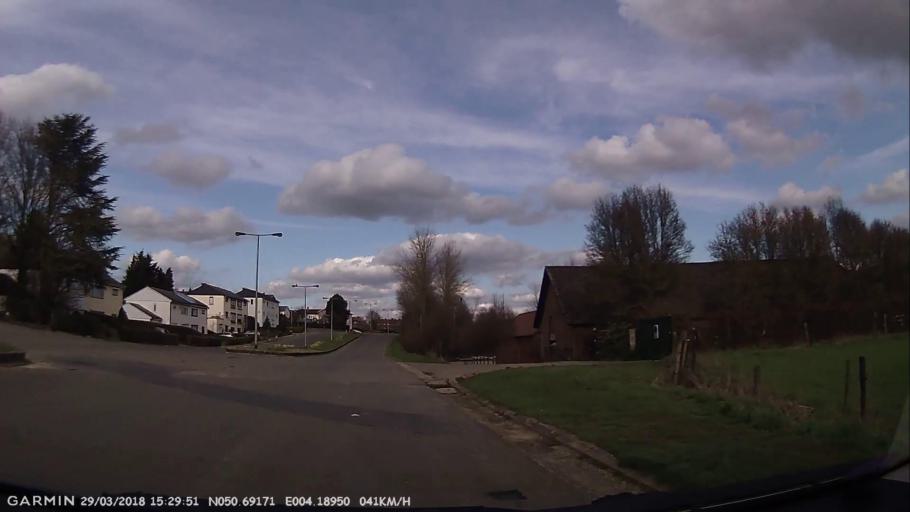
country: BE
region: Wallonia
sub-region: Province du Brabant Wallon
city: Tubize
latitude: 50.6917
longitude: 4.1895
